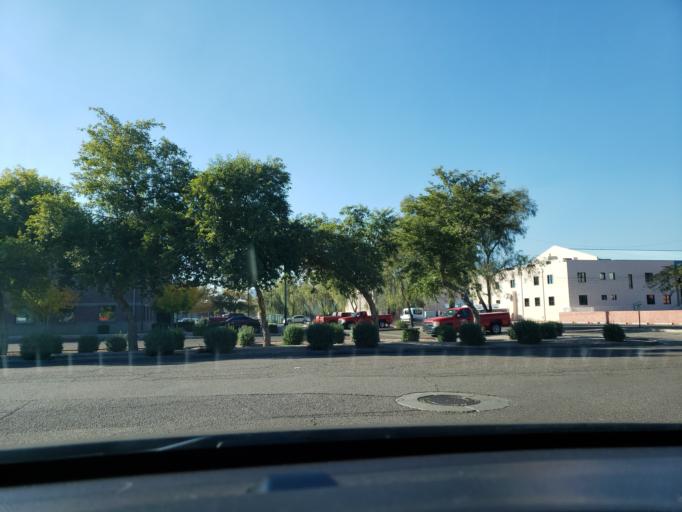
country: US
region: Arizona
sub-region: Maricopa County
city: Phoenix
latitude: 33.4462
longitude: -112.0563
